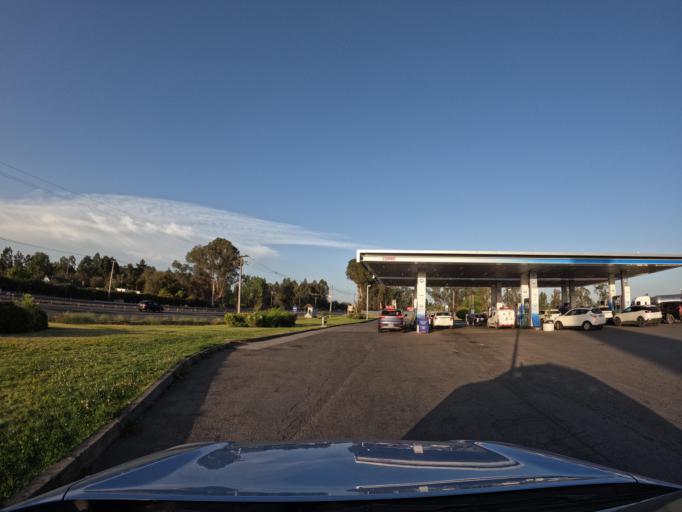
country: CL
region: Maule
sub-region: Provincia de Talca
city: Talca
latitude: -35.3206
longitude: -71.5393
